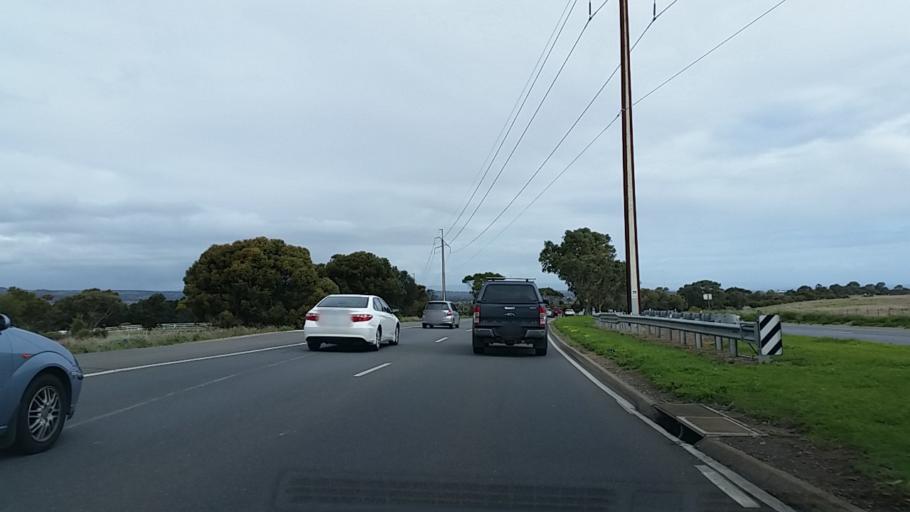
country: AU
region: South Australia
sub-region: Marion
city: Trott Park
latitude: -35.0604
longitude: 138.5354
